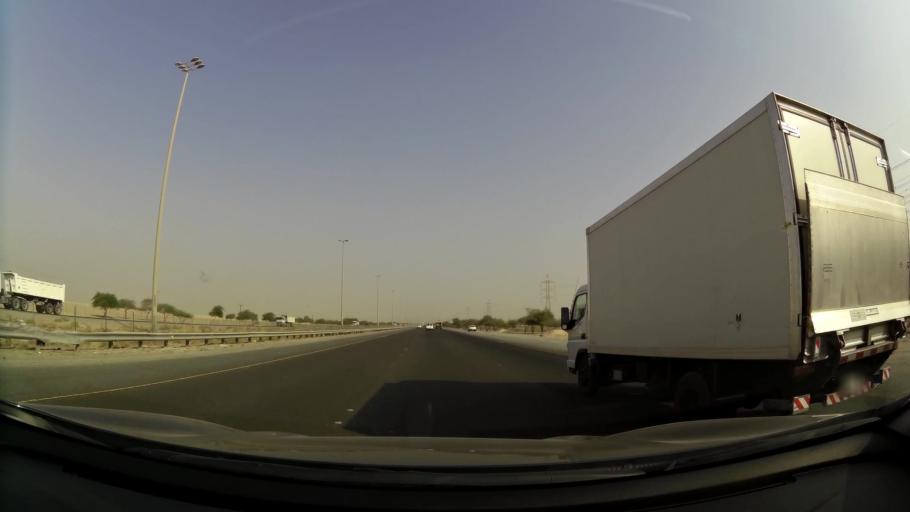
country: KW
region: Al Asimah
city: Ar Rabiyah
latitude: 29.2089
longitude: 47.8846
